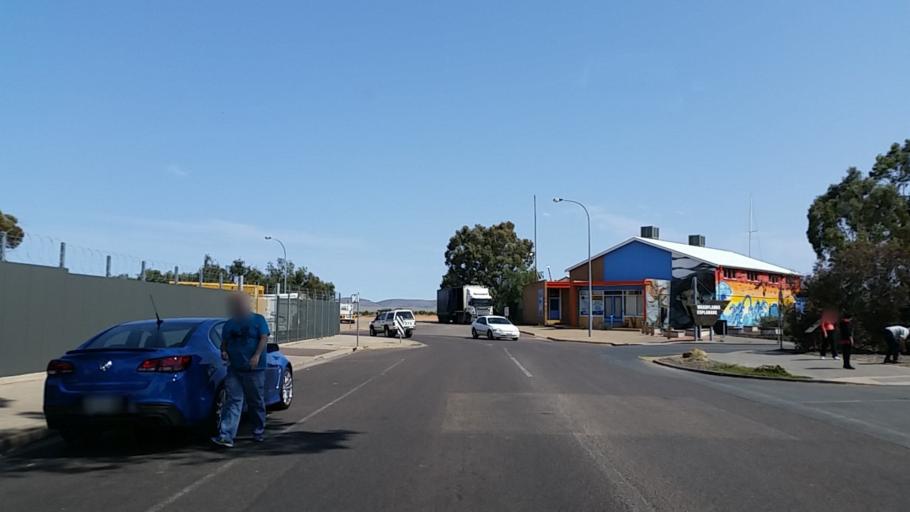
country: AU
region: South Australia
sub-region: Port Augusta
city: Port Augusta West
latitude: -32.4911
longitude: 137.7606
